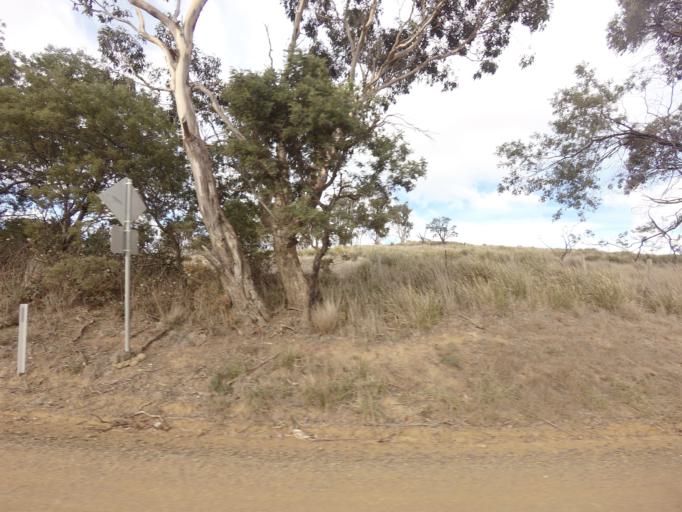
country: AU
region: Tasmania
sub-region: Brighton
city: Bridgewater
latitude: -42.4108
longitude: 147.3999
